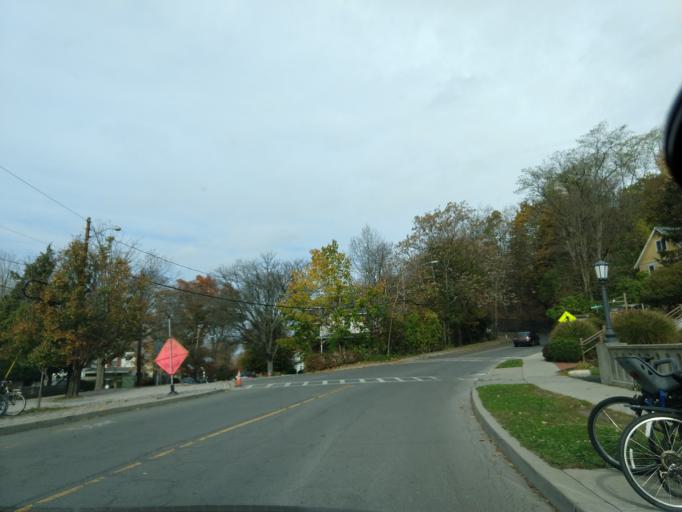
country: US
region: New York
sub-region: Tompkins County
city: Ithaca
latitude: 42.4431
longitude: -76.4945
